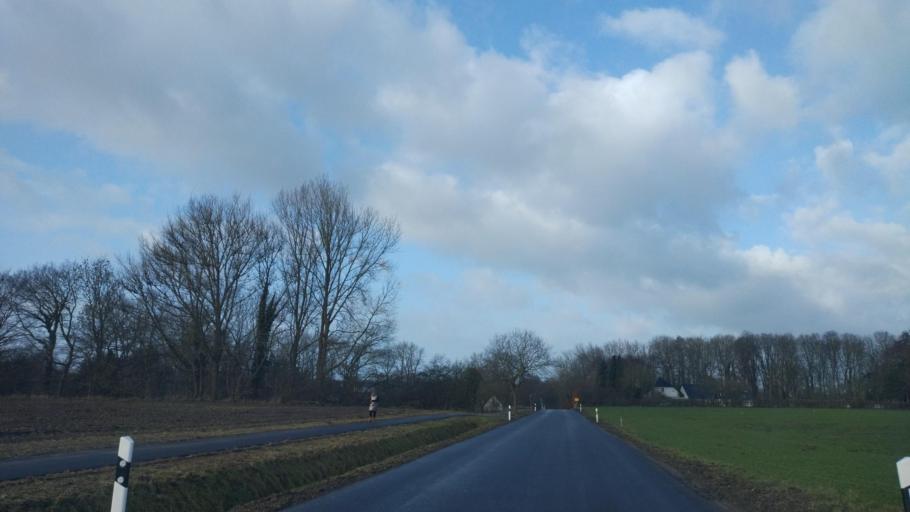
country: DE
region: Schleswig-Holstein
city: Taarstedt
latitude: 54.5617
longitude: 9.6851
